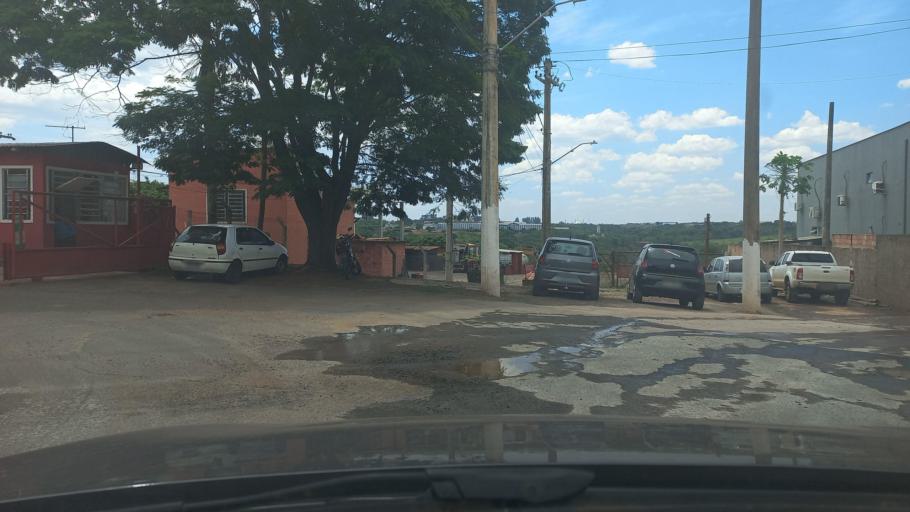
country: BR
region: Minas Gerais
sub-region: Uberaba
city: Uberaba
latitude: -19.7319
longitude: -47.9773
